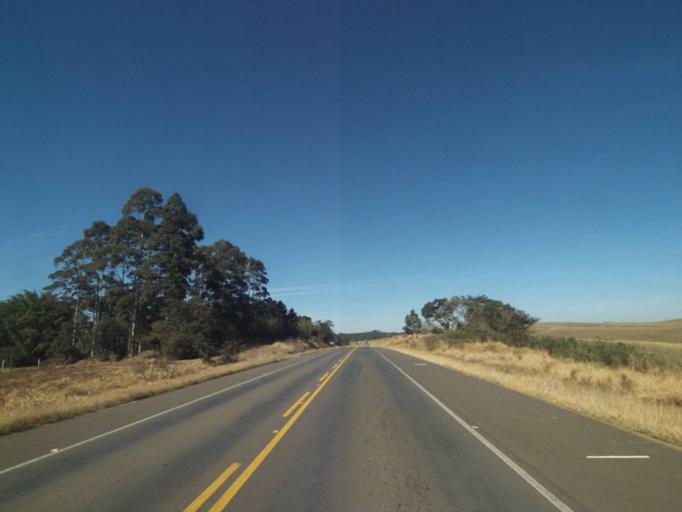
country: BR
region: Parana
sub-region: Tibagi
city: Tibagi
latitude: -24.7671
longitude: -50.4683
